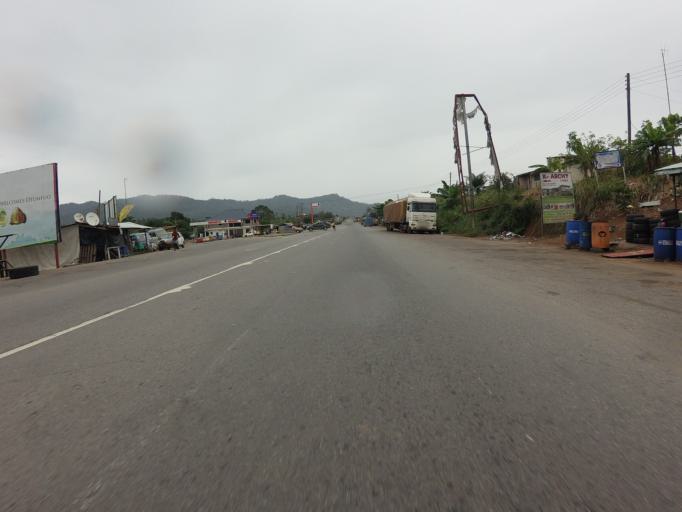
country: GH
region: Eastern
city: Suhum
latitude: 6.1124
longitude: -0.4891
